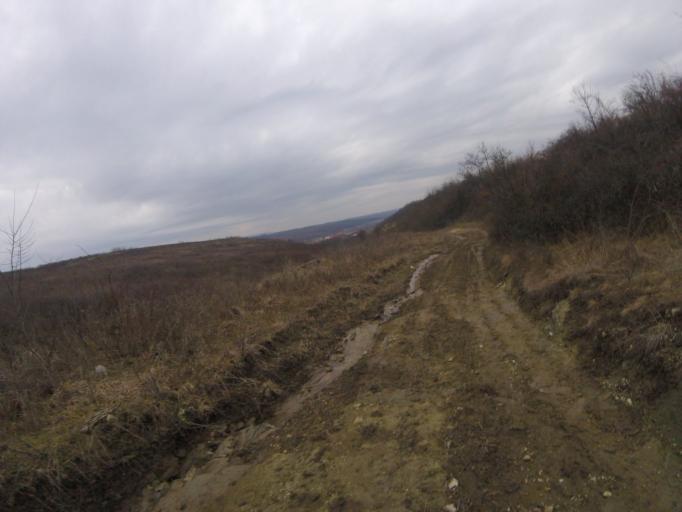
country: HU
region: Heves
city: Kerecsend
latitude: 47.8317
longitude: 20.3470
